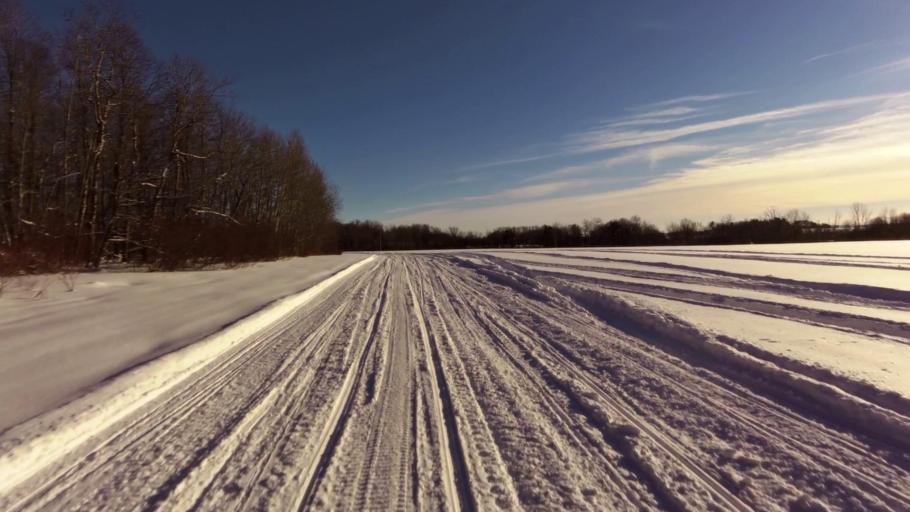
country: US
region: New York
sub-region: Chautauqua County
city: Mayville
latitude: 42.2460
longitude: -79.3960
